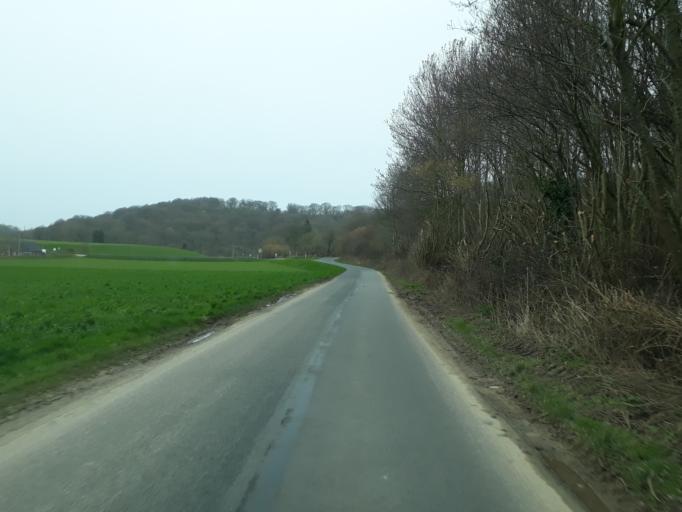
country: FR
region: Haute-Normandie
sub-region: Departement de la Seine-Maritime
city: Les Loges
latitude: 49.6765
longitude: 0.2582
